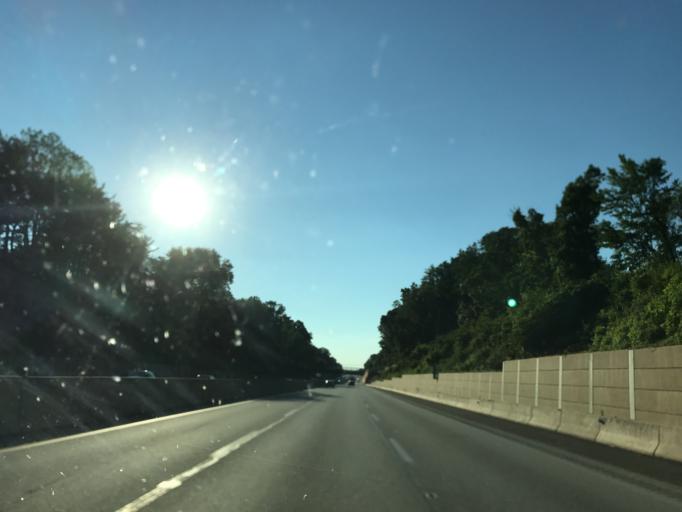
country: US
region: Pennsylvania
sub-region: Bucks County
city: Feasterville
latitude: 40.1542
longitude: -75.0316
